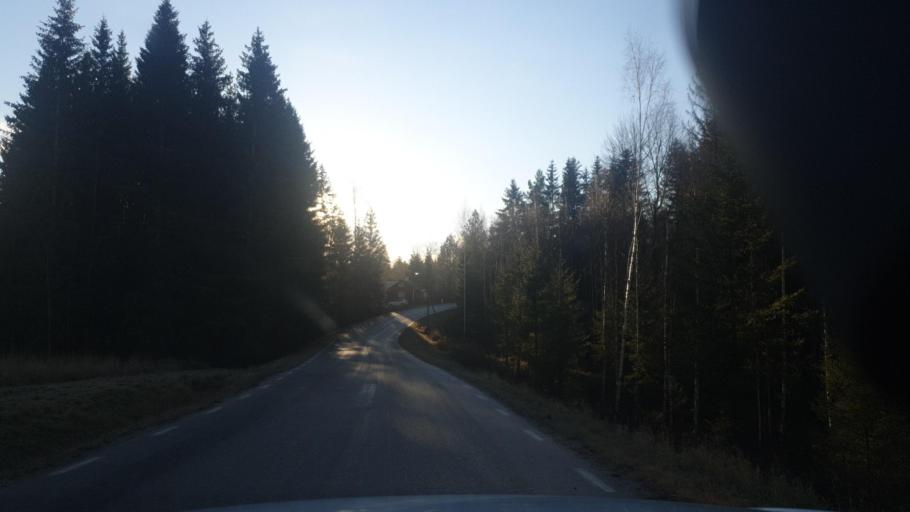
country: SE
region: Vaermland
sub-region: Karlstads Kommun
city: Edsvalla
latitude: 59.5667
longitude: 13.0537
